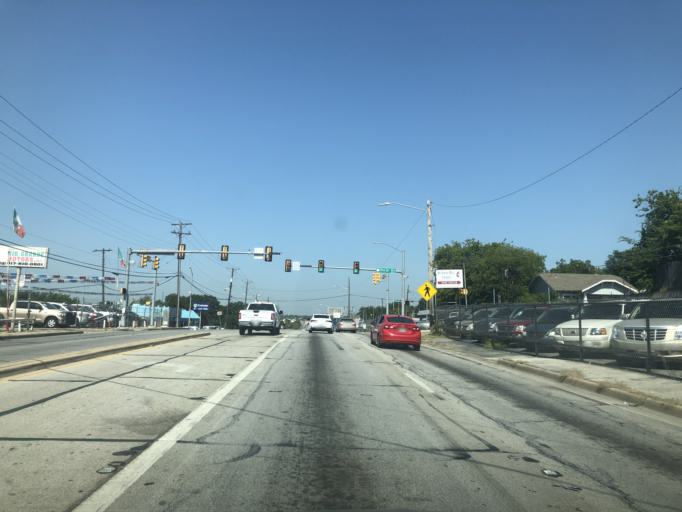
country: US
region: Texas
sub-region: Tarrant County
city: Haltom City
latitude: 32.7953
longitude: -97.3308
